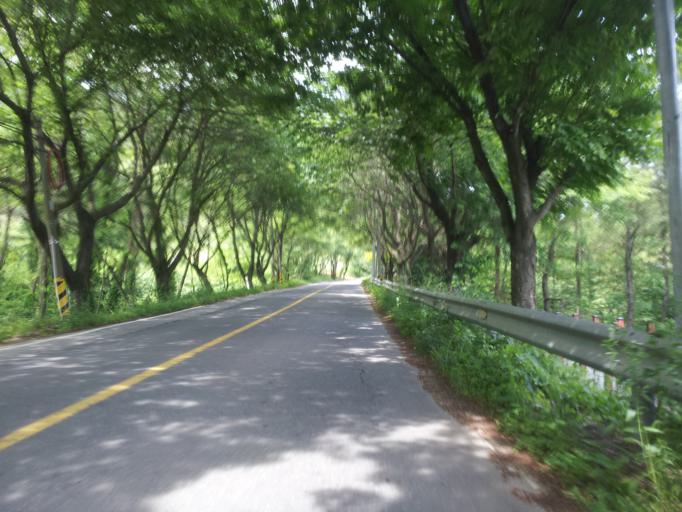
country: KR
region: Daejeon
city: Sintansin
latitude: 36.4312
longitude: 127.4681
